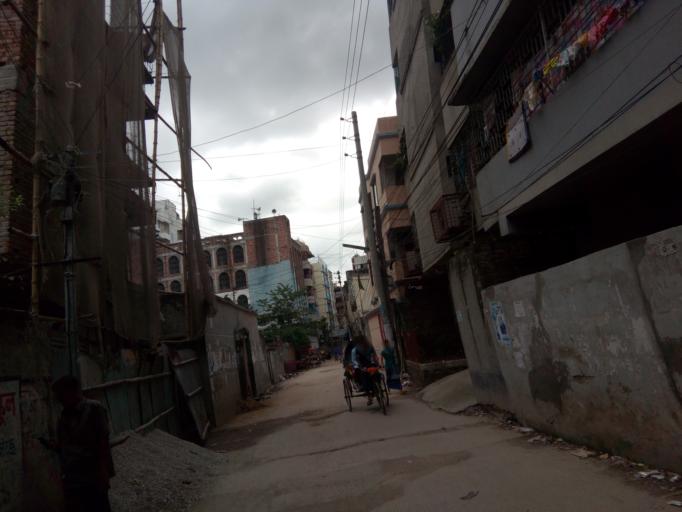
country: BD
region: Dhaka
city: Azimpur
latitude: 23.7679
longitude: 90.3534
